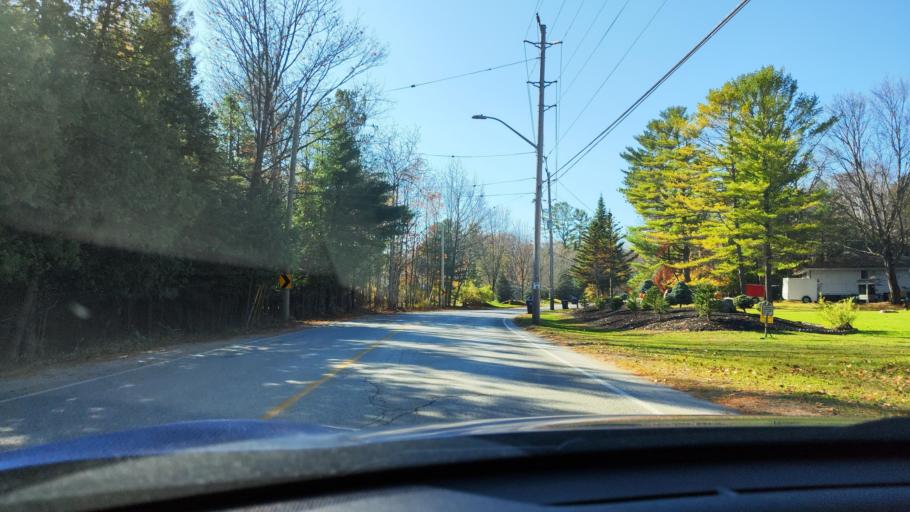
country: CA
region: Ontario
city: Wasaga Beach
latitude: 44.4975
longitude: -79.9998
